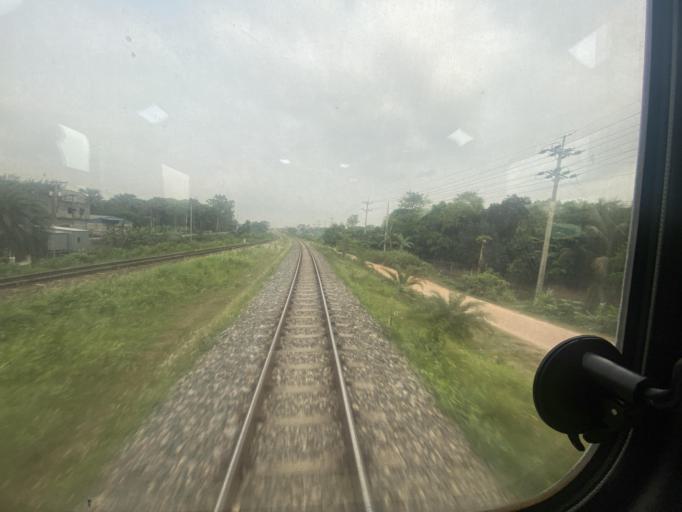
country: BD
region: Dhaka
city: Tungi
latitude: 23.9365
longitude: 90.4847
